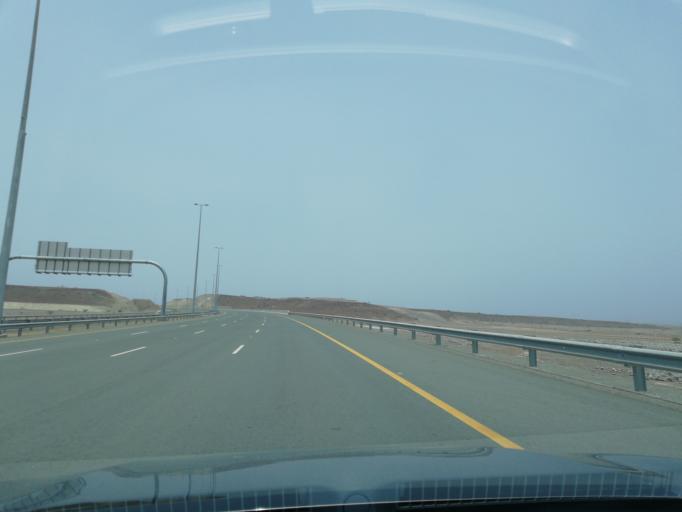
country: OM
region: Al Batinah
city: Al Liwa'
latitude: 24.5370
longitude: 56.4991
